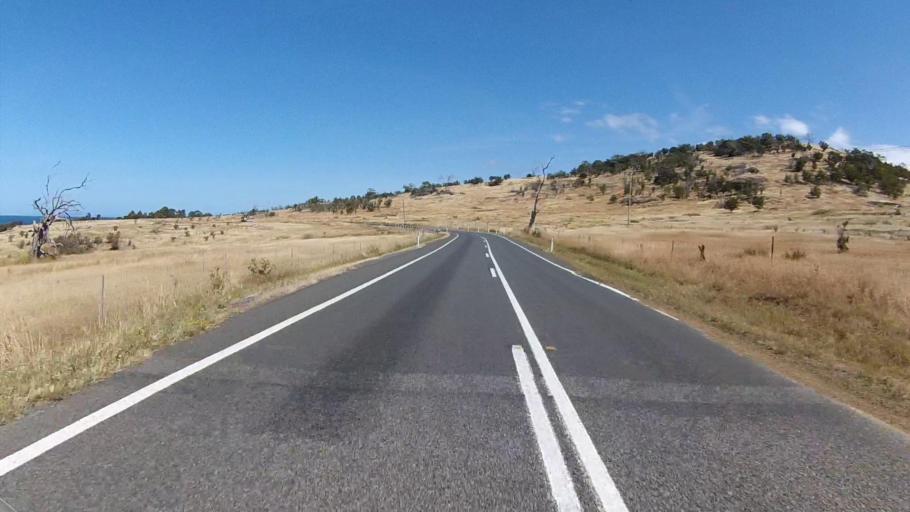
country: AU
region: Tasmania
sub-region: Sorell
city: Sorell
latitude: -42.1785
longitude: 148.0681
